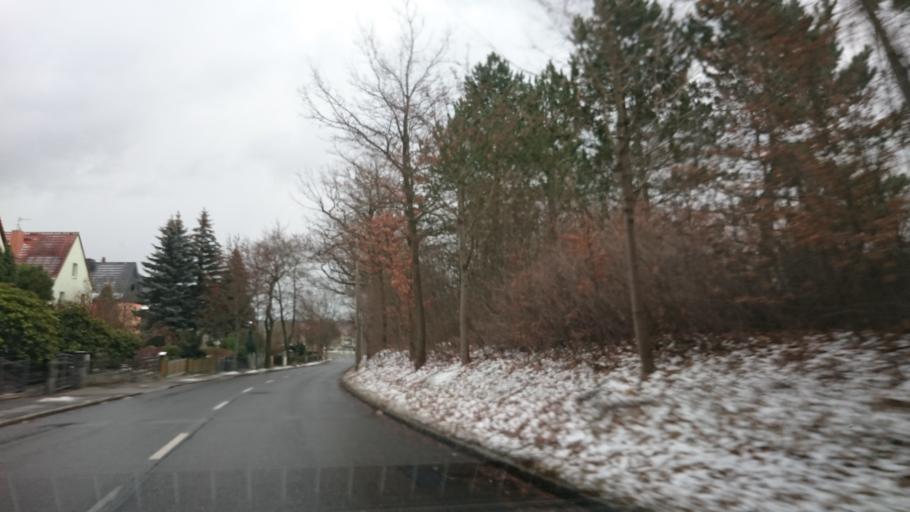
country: DE
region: Saxony
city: Weissenborn
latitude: 50.7259
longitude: 12.4597
